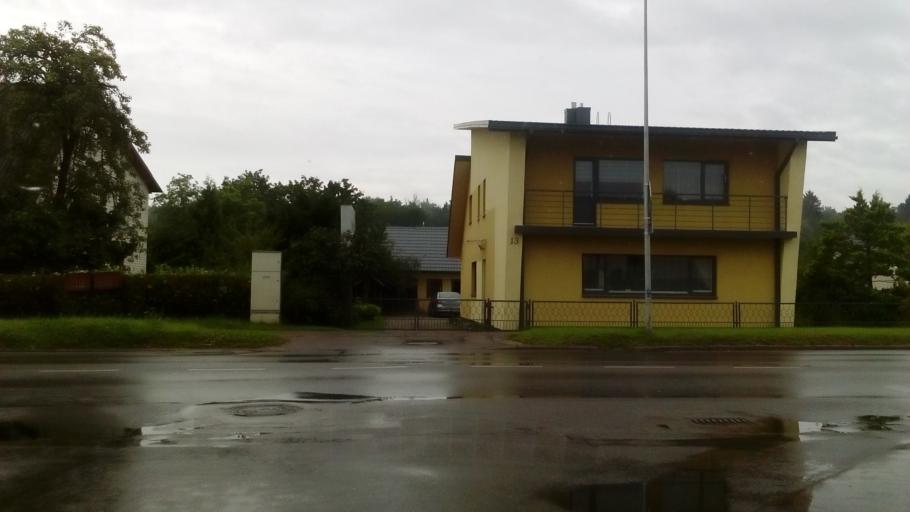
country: LT
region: Alytaus apskritis
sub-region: Alytus
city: Alytus
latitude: 54.3871
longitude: 24.0402
